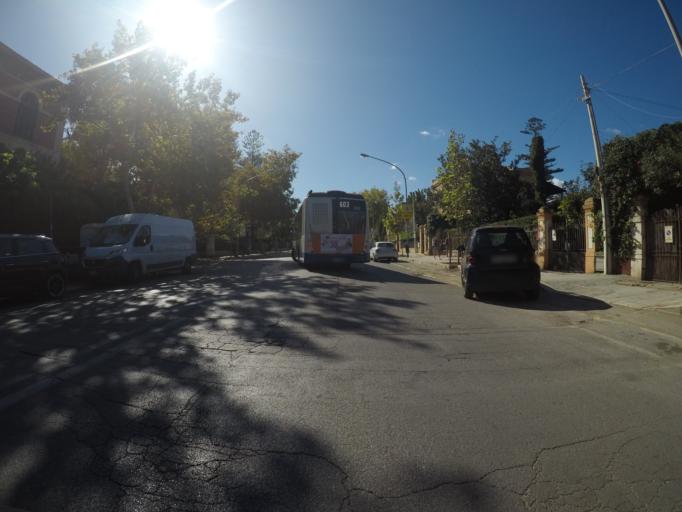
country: IT
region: Sicily
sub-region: Palermo
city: Palermo
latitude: 38.1963
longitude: 13.3319
